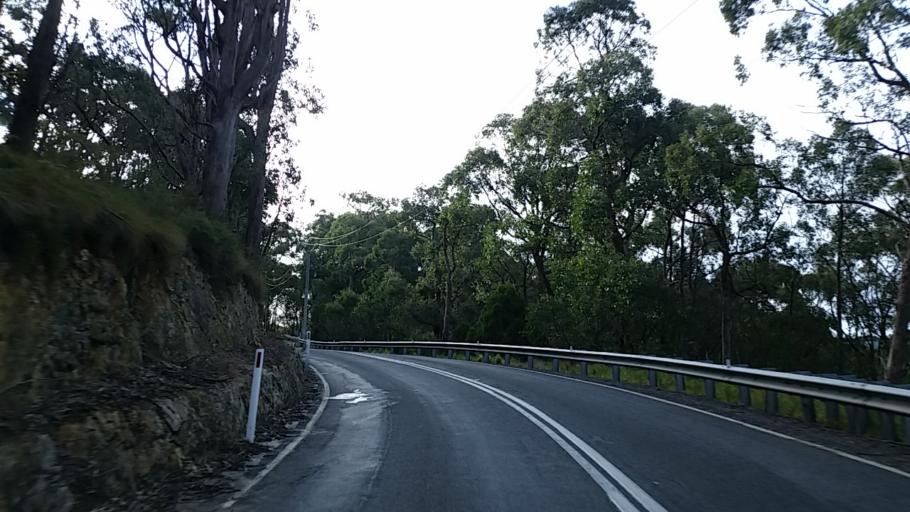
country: AU
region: South Australia
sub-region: Adelaide Hills
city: Bridgewater
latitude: -34.9636
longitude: 138.7563
